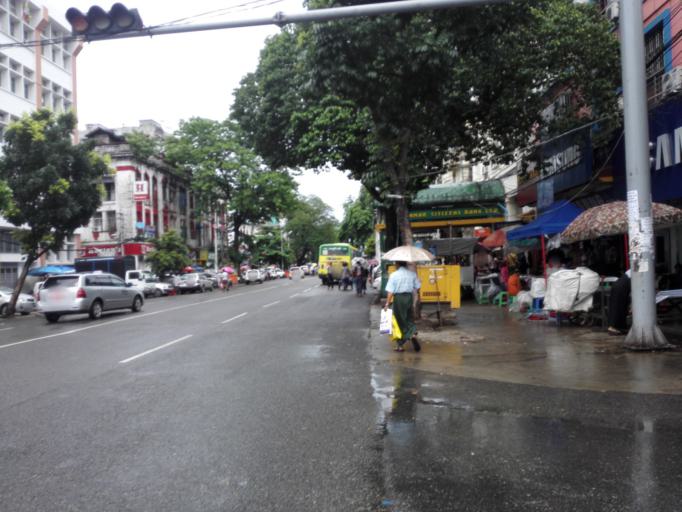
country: MM
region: Yangon
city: Yangon
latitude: 16.7742
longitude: 96.1618
